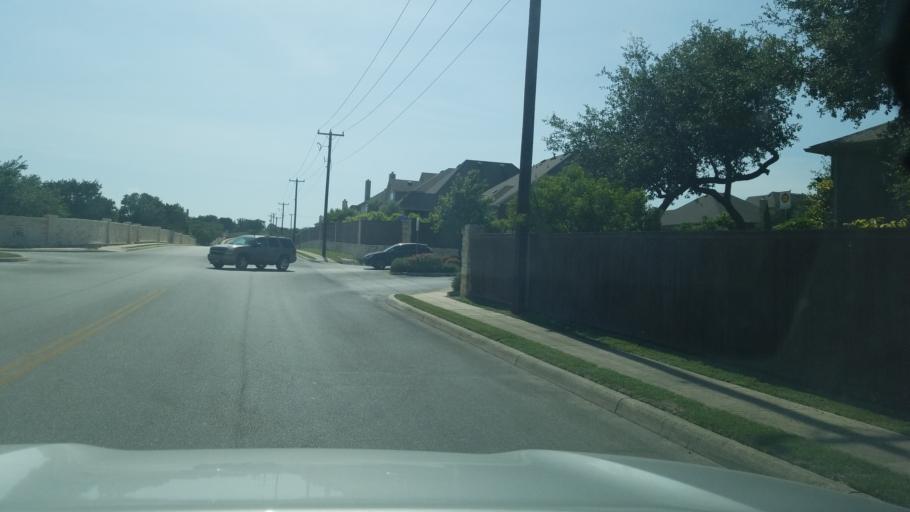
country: US
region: Texas
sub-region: Bexar County
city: Timberwood Park
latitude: 29.6689
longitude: -98.4534
